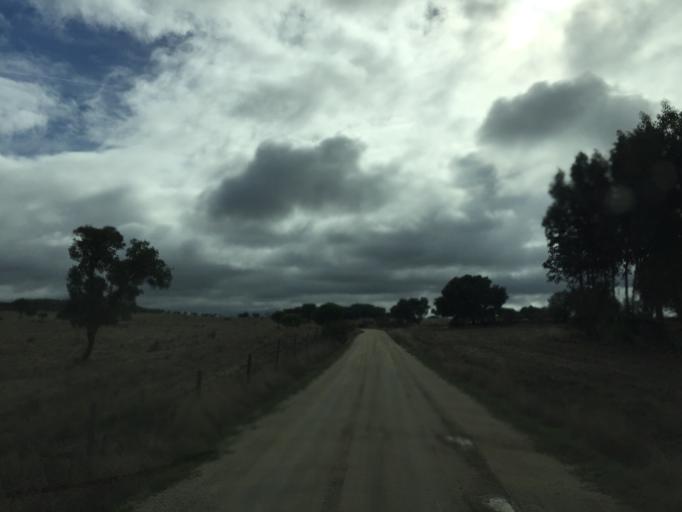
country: PT
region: Portalegre
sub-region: Alter do Chao
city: Alter do Chao
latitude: 39.2401
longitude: -7.7004
